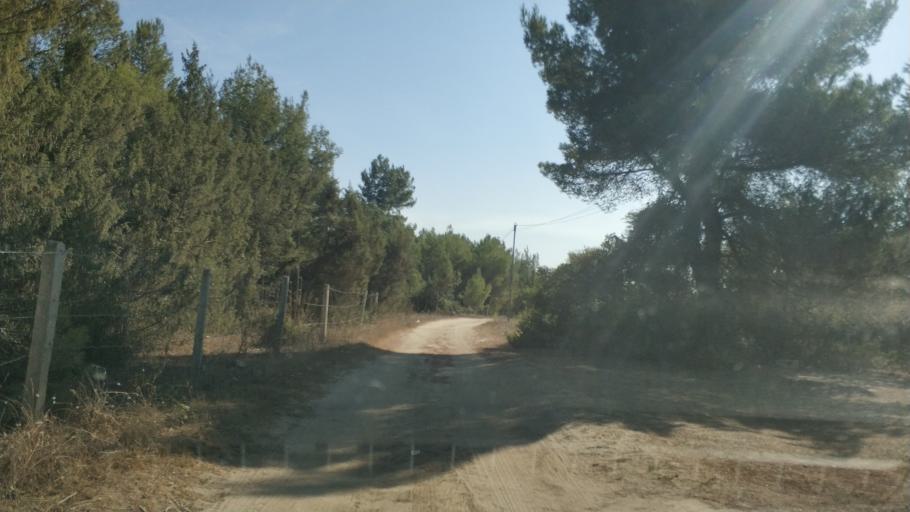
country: AL
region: Fier
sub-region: Rrethi i Lushnjes
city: Divjake
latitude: 40.9626
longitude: 19.4765
